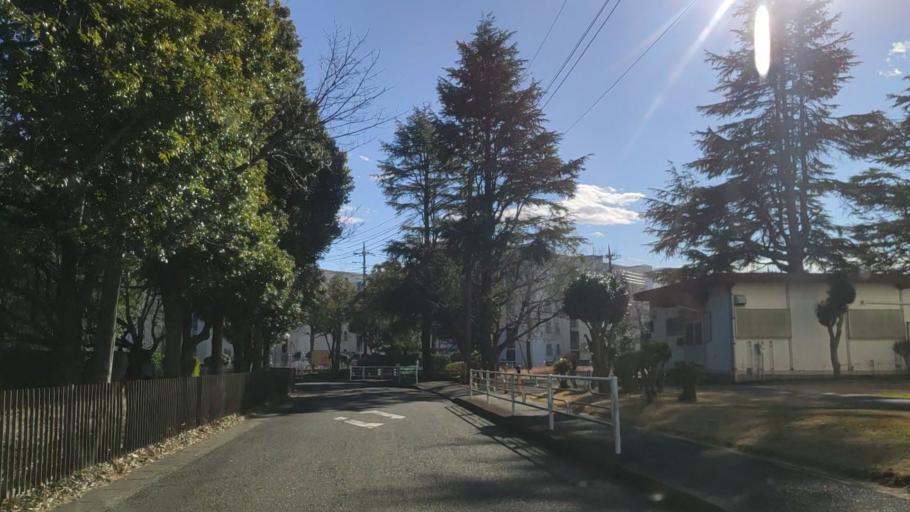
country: JP
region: Kanagawa
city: Minami-rinkan
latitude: 35.5010
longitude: 139.5311
